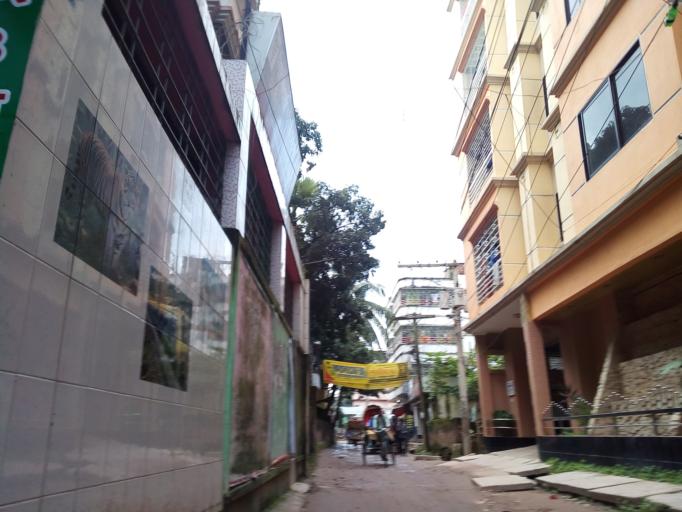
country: BD
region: Dhaka
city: Tungi
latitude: 23.8414
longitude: 90.2540
